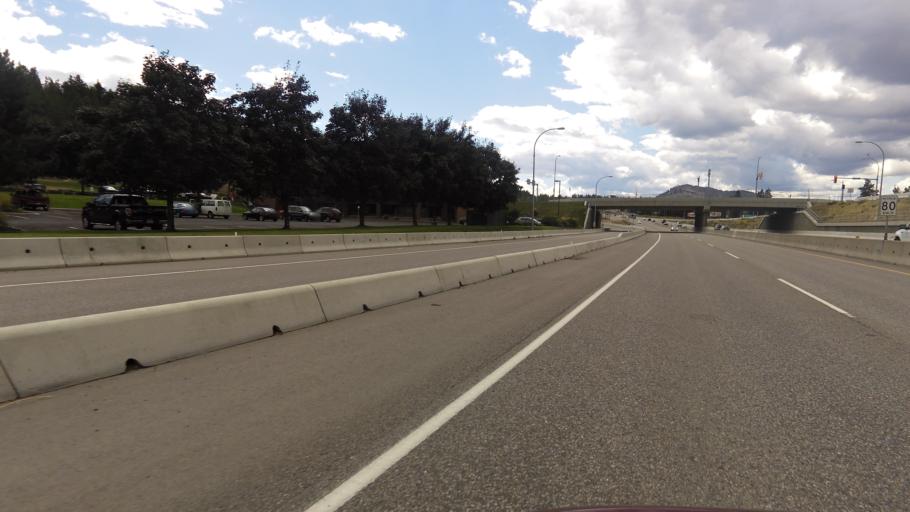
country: CA
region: British Columbia
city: Kelowna
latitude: 49.8828
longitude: -119.5343
